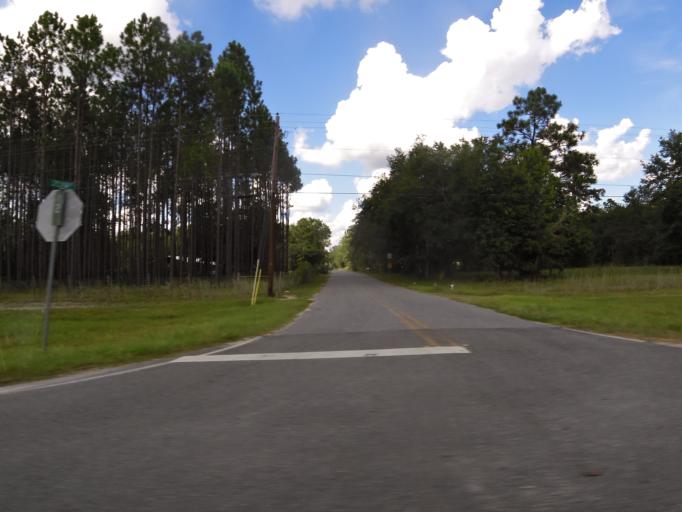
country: US
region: Georgia
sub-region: Echols County
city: Statenville
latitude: 30.7019
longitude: -83.0081
